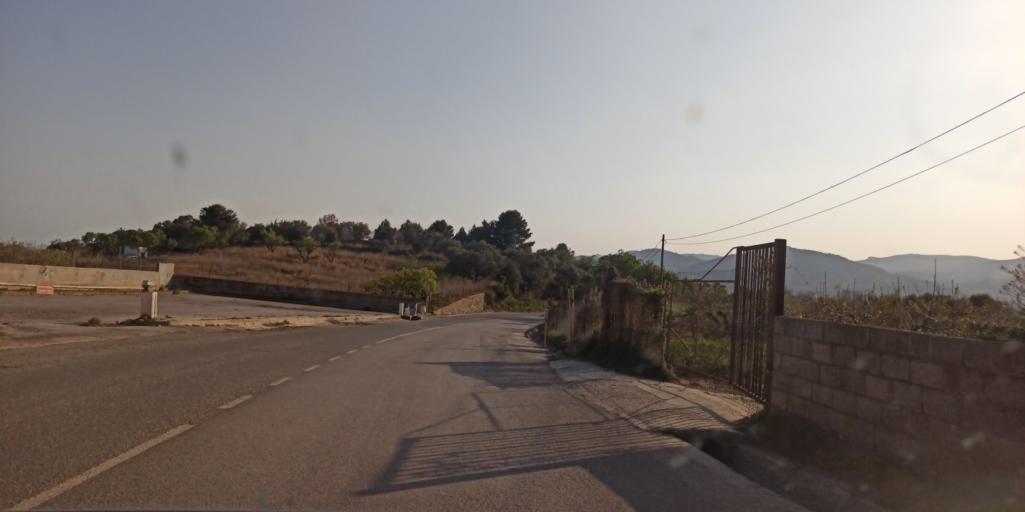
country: ES
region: Catalonia
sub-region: Provincia de Barcelona
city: Sant Feliu de Llobregat
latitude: 41.3978
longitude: 2.0540
